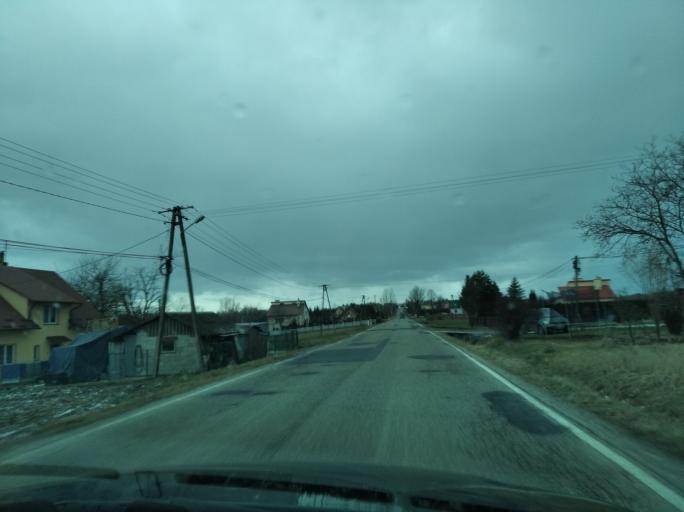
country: PL
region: Subcarpathian Voivodeship
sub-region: Powiat rzeszowski
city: Hyzne
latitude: 49.9242
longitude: 22.1959
